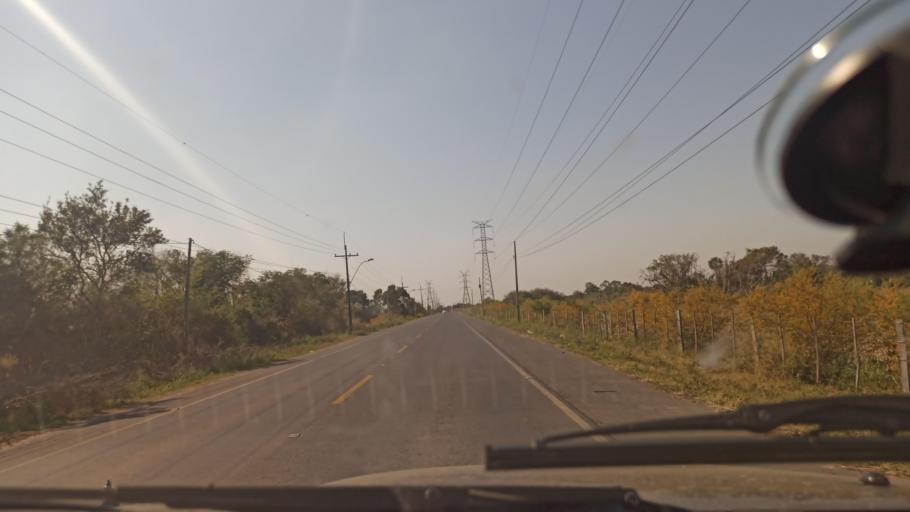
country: PY
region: Presidente Hayes
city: Nanawa
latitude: -25.2489
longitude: -57.6693
